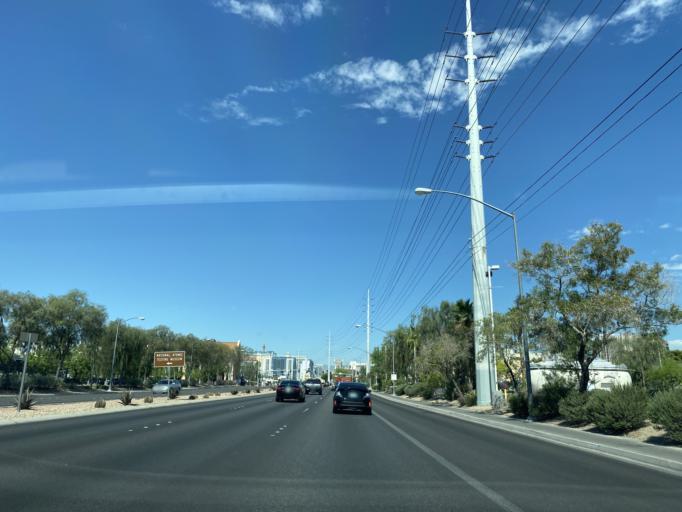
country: US
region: Nevada
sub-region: Clark County
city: Paradise
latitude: 36.1148
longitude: -115.1482
